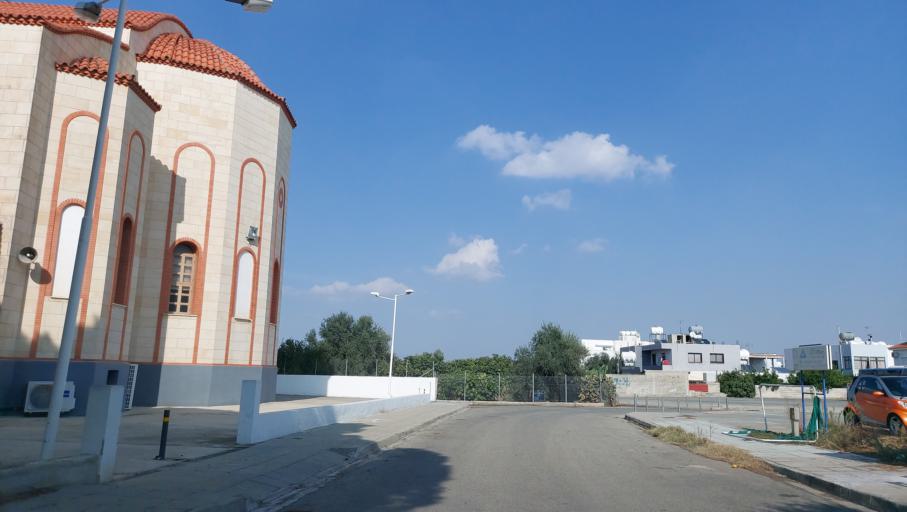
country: CY
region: Lefkosia
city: Kato Deftera
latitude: 35.1058
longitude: 33.3041
